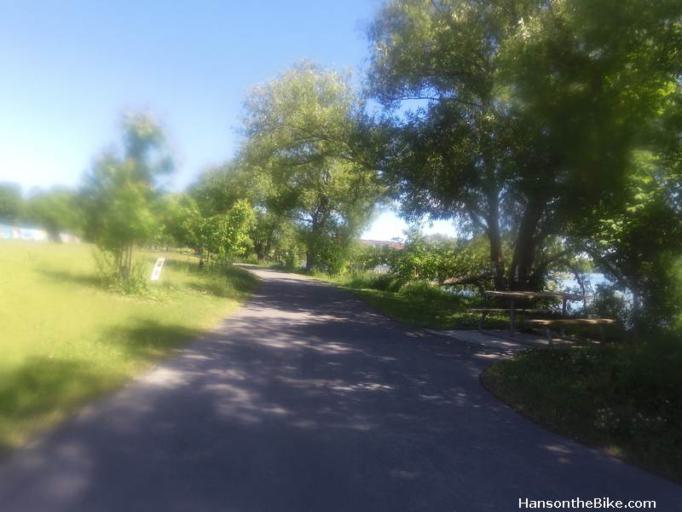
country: CA
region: Ontario
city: Kingston
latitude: 44.2386
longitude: -76.4810
